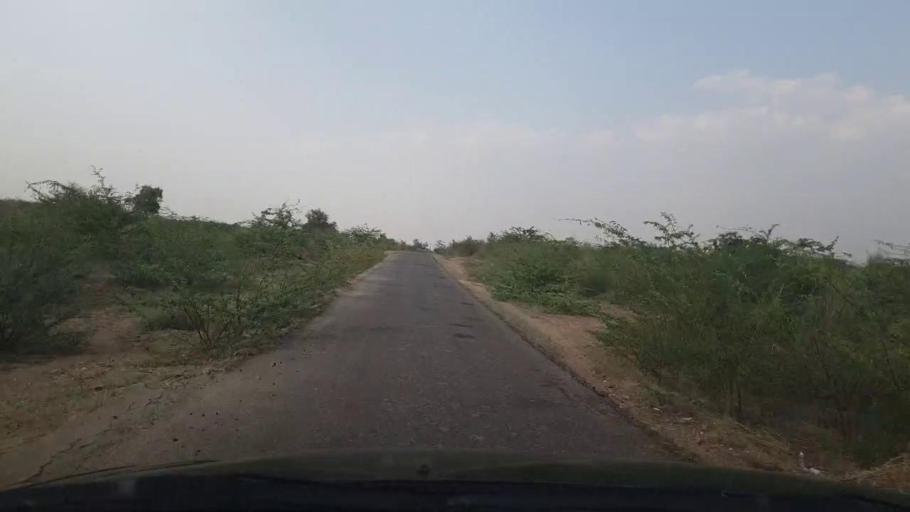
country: PK
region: Sindh
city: Islamkot
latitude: 25.0367
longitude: 70.5552
